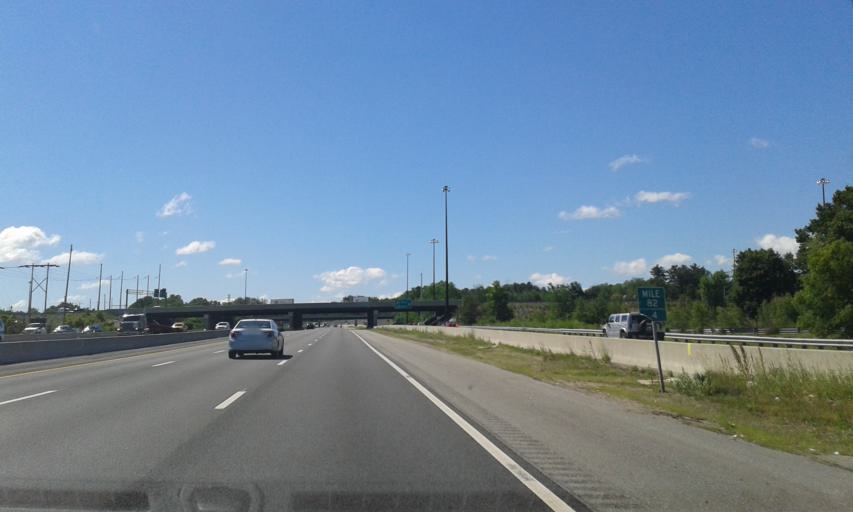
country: US
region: Massachusetts
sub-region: Middlesex County
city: Lowell
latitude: 42.6096
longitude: -71.3268
